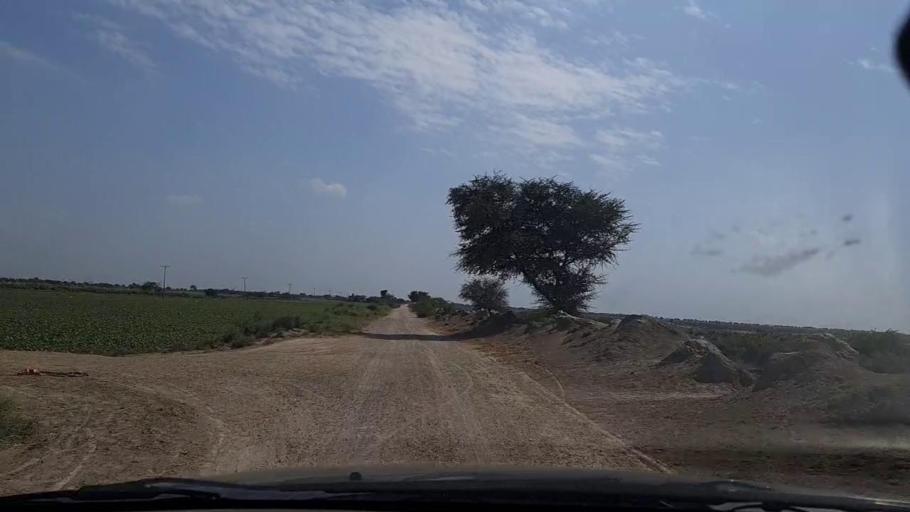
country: PK
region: Sindh
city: Mirpur Batoro
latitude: 24.5806
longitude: 68.1955
